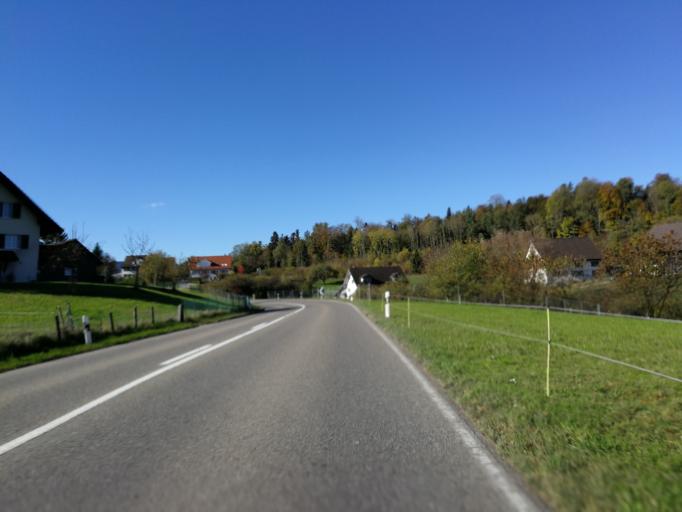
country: CH
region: Zurich
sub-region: Bezirk Hinwil
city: Binzikon
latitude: 47.2873
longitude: 8.7452
